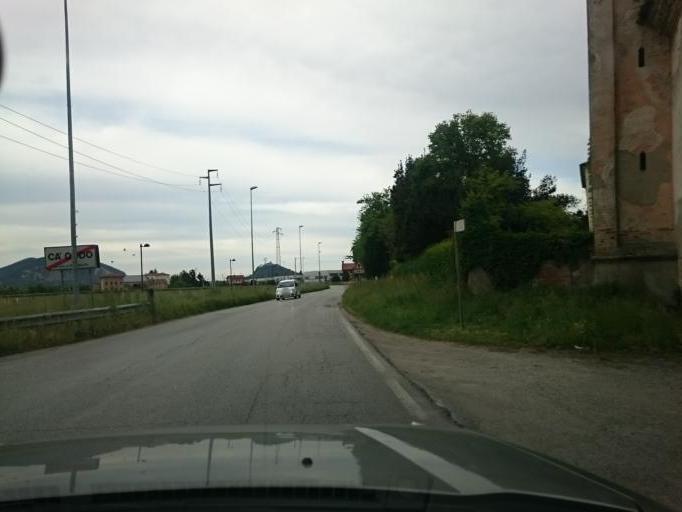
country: IT
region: Veneto
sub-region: Provincia di Padova
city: Monselice
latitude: 45.2145
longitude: 11.7360
